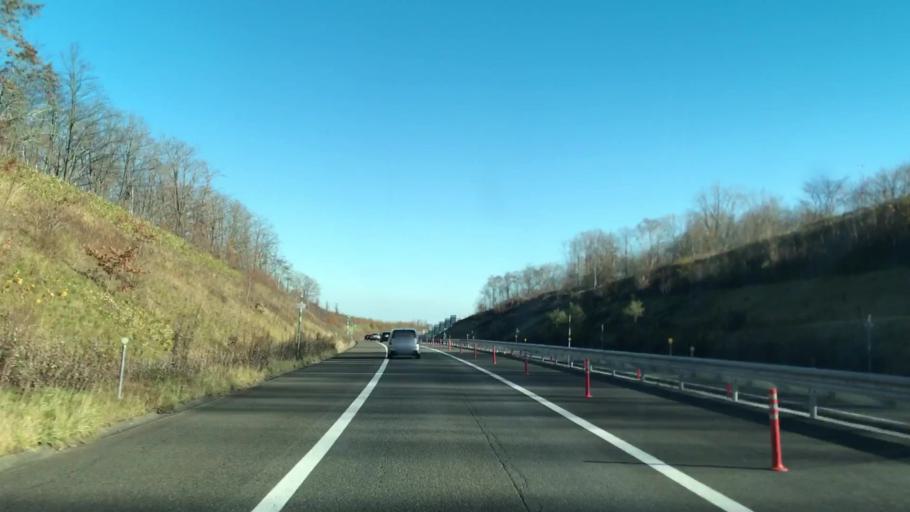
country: JP
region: Hokkaido
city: Otofuke
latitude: 43.0331
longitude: 142.7940
